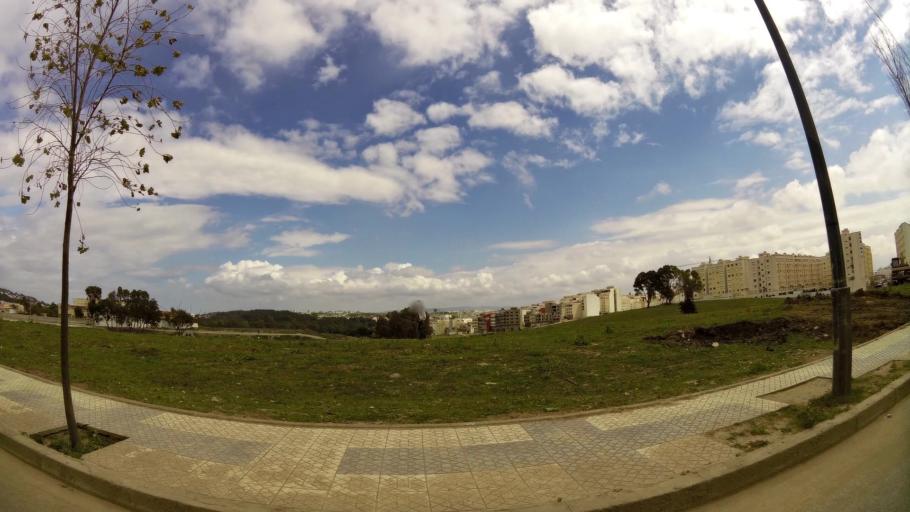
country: MA
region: Tanger-Tetouan
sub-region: Tanger-Assilah
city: Boukhalef
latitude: 35.7687
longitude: -5.8591
